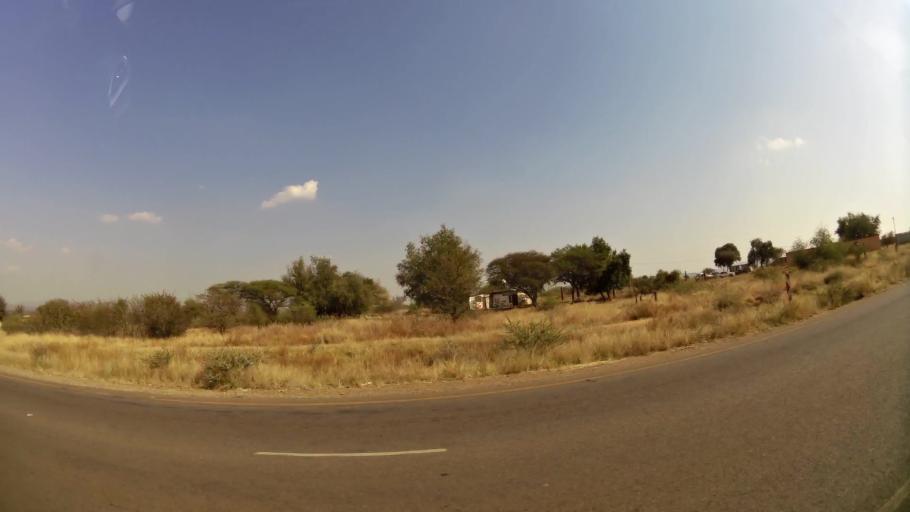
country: ZA
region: North-West
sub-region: Bojanala Platinum District Municipality
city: Mogwase
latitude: -25.3839
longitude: 27.0675
